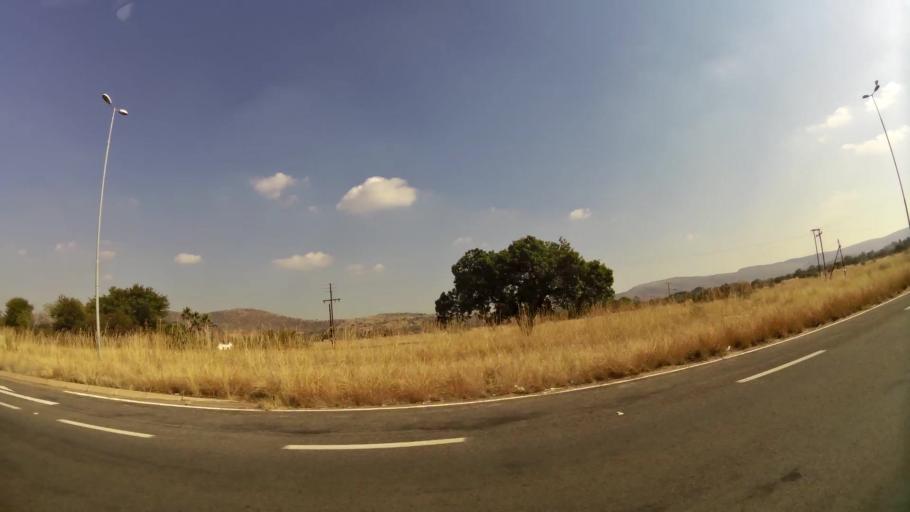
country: ZA
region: North-West
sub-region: Bojanala Platinum District Municipality
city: Rustenburg
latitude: -25.5276
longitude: 27.1126
